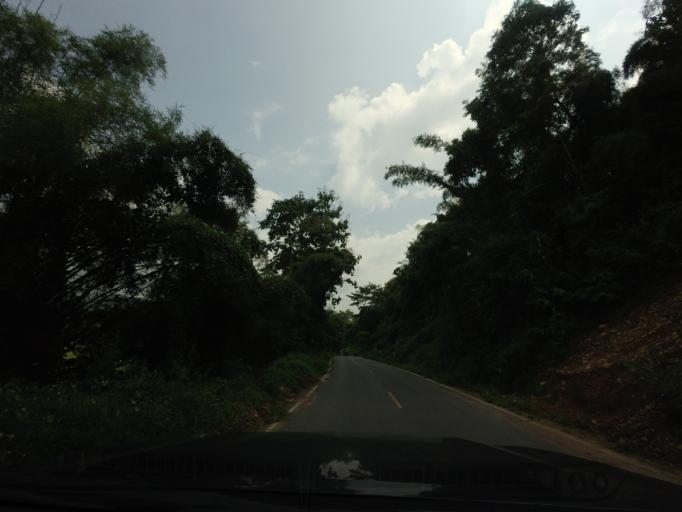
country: TH
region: Nan
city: Pua
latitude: 19.1686
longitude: 100.9292
